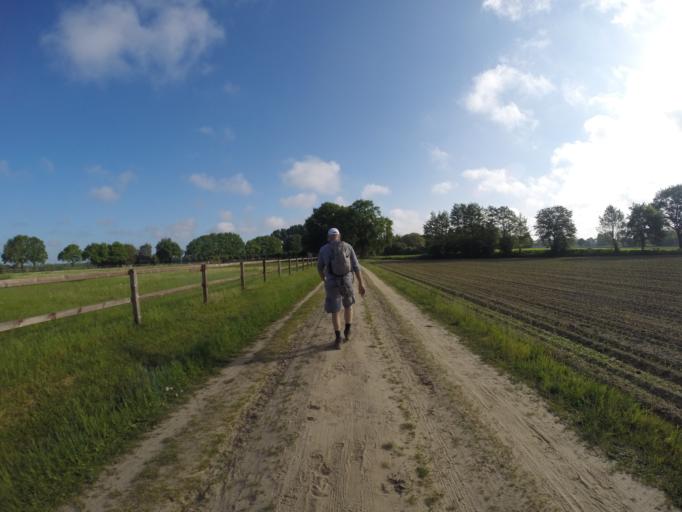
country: NL
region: Gelderland
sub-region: Oude IJsselstreek
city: Wisch
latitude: 51.9386
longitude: 6.3671
